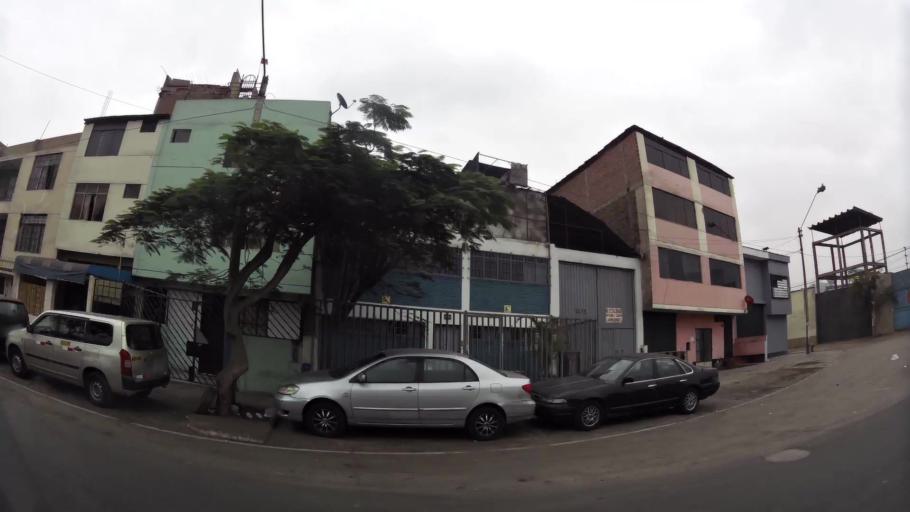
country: PE
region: Lima
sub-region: Lima
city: San Luis
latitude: -12.0748
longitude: -76.9927
